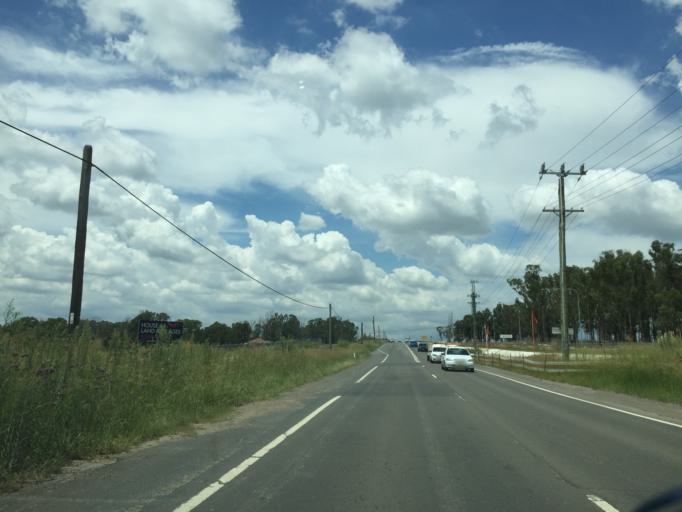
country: AU
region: New South Wales
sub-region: Blacktown
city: Hassall Grove
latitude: -33.7097
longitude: 150.8407
